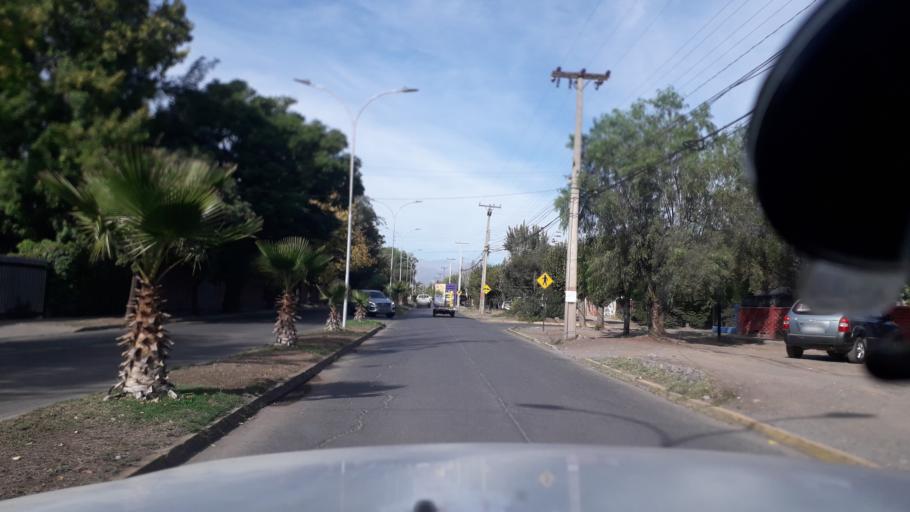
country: CL
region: Valparaiso
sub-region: Provincia de San Felipe
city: San Felipe
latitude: -32.7488
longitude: -70.7152
